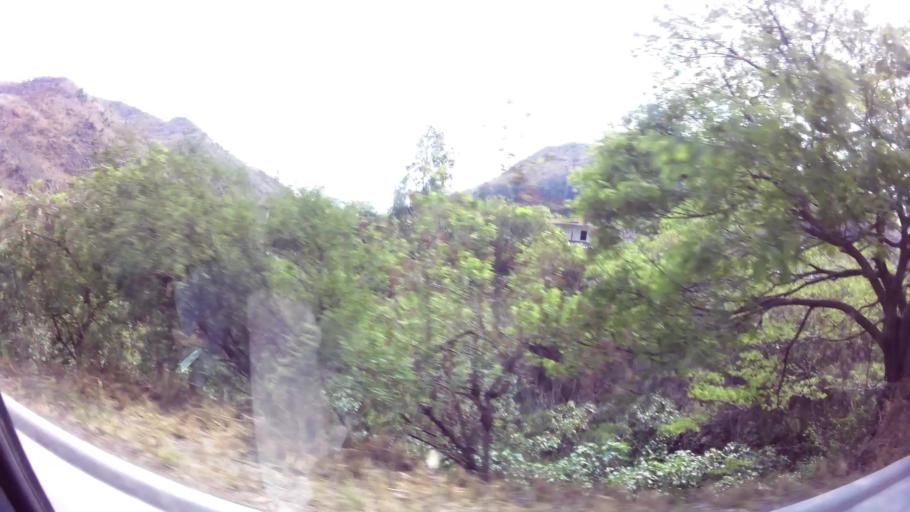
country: HN
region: Francisco Morazan
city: Tegucigalpa
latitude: 14.1173
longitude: -87.2179
